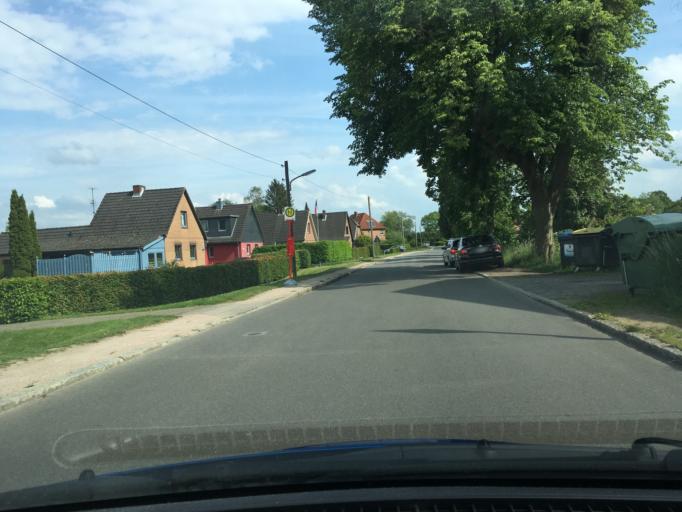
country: DE
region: Hamburg
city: Bergedorf
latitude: 53.4715
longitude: 10.2325
